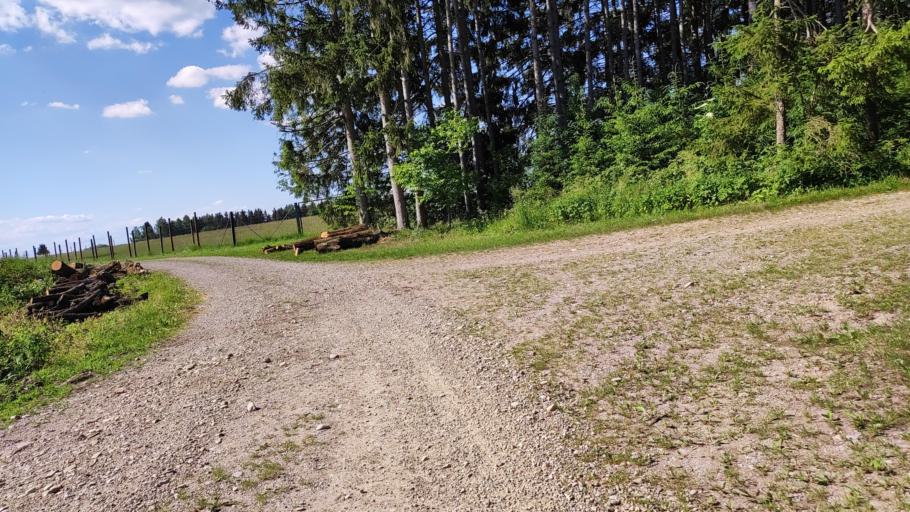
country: DE
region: Bavaria
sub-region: Swabia
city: Dinkelscherben
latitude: 48.3689
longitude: 10.5977
